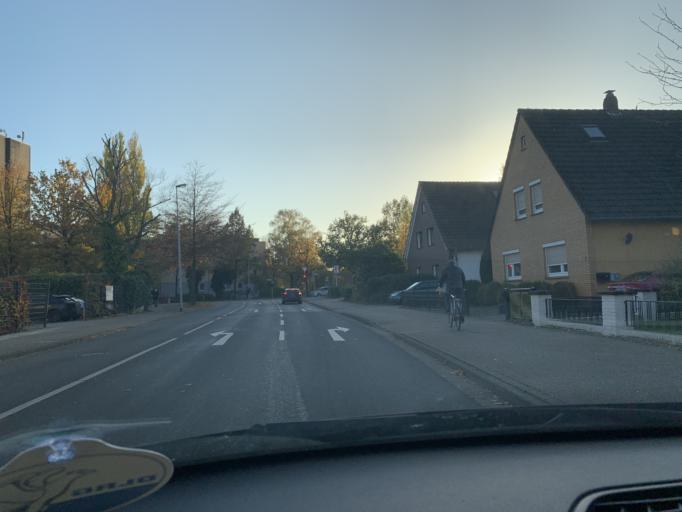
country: DE
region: Lower Saxony
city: Oldenburg
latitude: 53.1418
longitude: 8.1760
